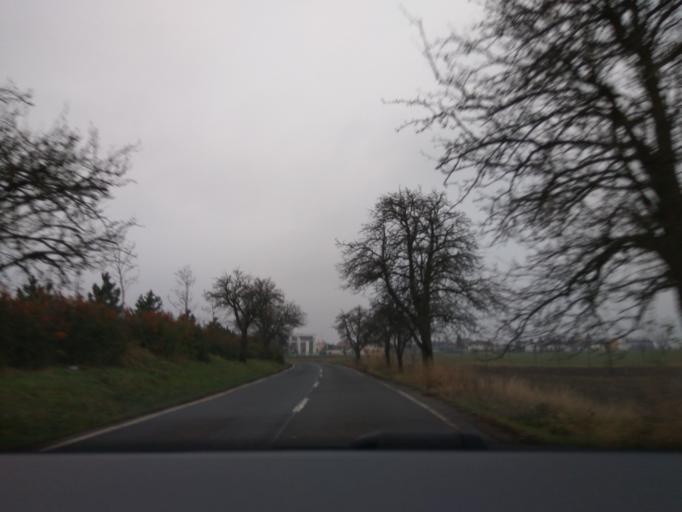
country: CZ
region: Praha
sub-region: Praha 19
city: Kbely
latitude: 50.1513
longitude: 14.5406
